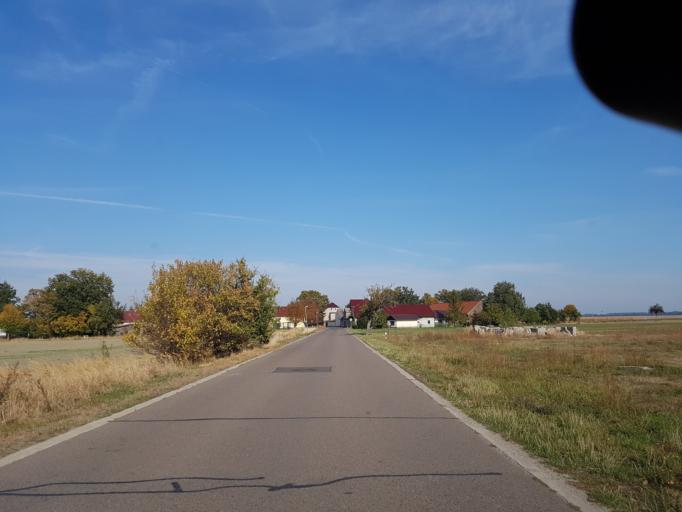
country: DE
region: Brandenburg
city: Doberlug-Kirchhain
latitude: 51.6679
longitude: 13.5097
